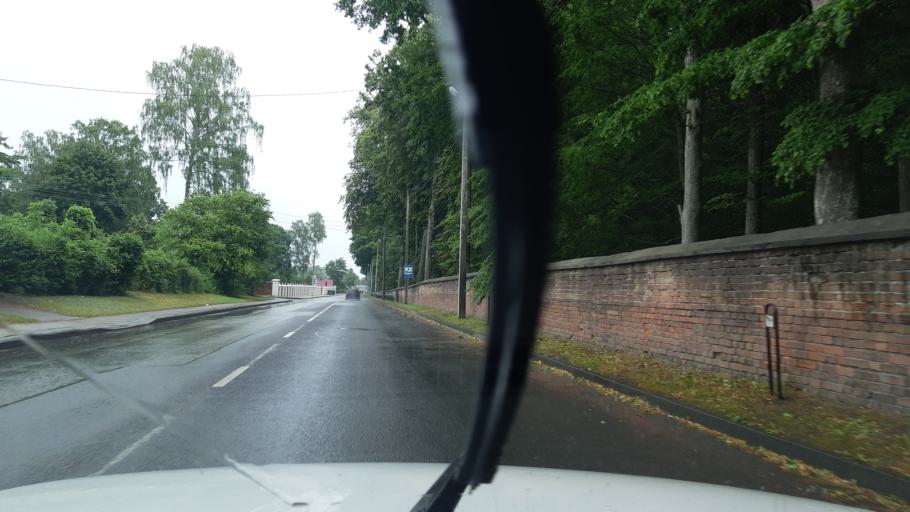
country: LT
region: Taurages apskritis
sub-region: Jurbarkas
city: Jurbarkas
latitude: 55.0824
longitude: 22.7508
